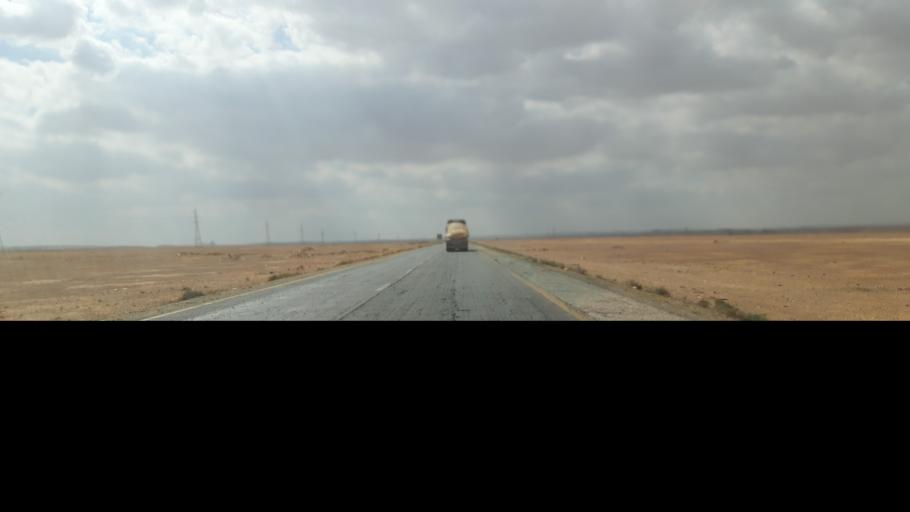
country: JO
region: Amman
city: Sahab
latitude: 31.7634
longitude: 36.2951
